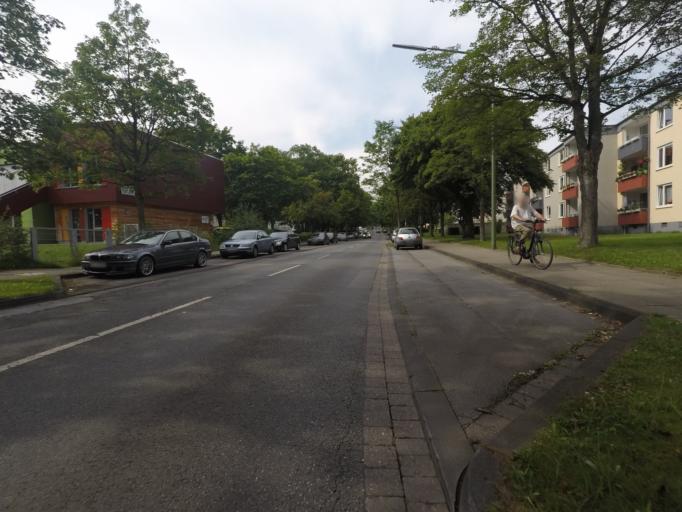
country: DE
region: North Rhine-Westphalia
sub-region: Regierungsbezirk Detmold
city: Bielefeld
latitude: 52.0475
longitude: 8.5967
